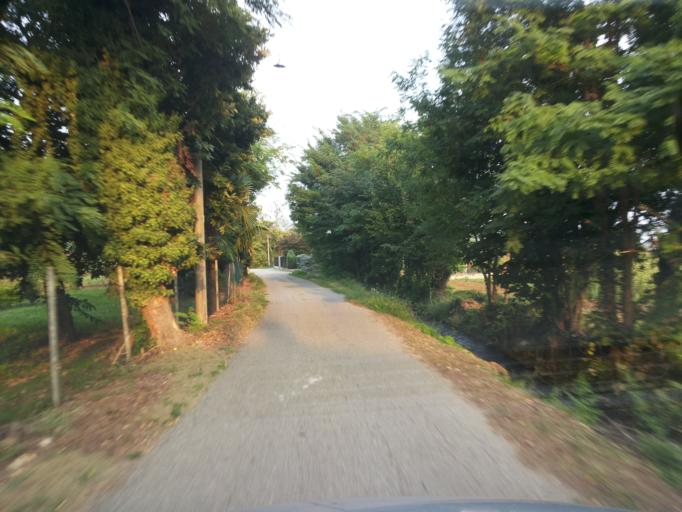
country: IT
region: Piedmont
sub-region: Provincia di Biella
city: Cavaglia
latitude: 45.3982
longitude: 8.0936
